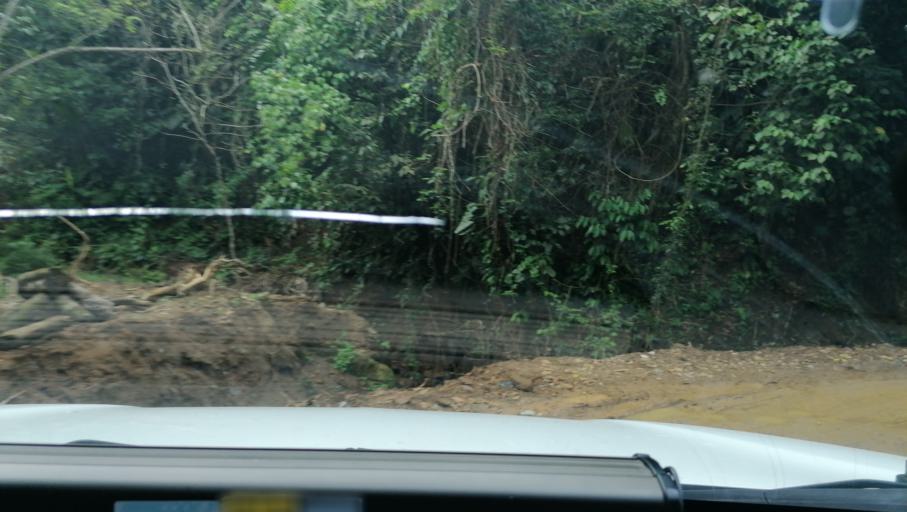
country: MX
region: Chiapas
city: Ixtacomitan
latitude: 17.3321
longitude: -93.1076
